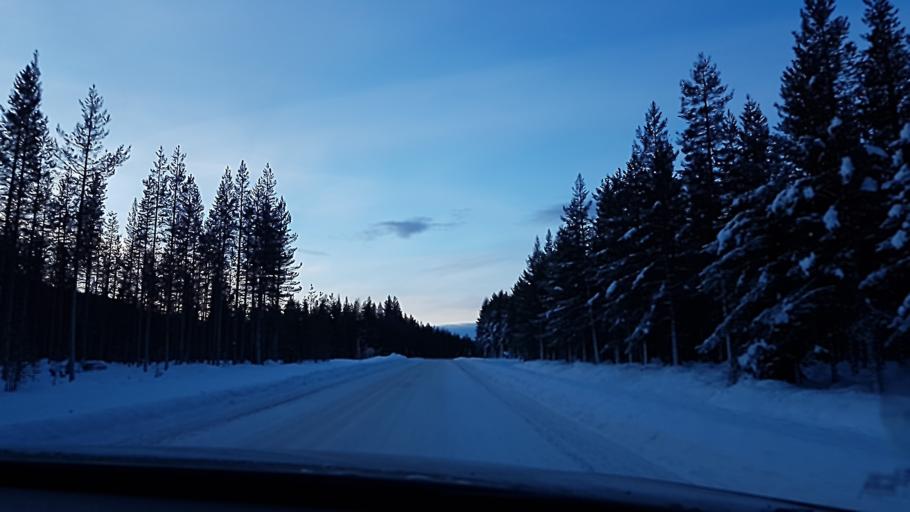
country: SE
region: Norrbotten
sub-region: Arvidsjaurs Kommun
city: Arvidsjaur
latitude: 65.9488
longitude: 19.5144
